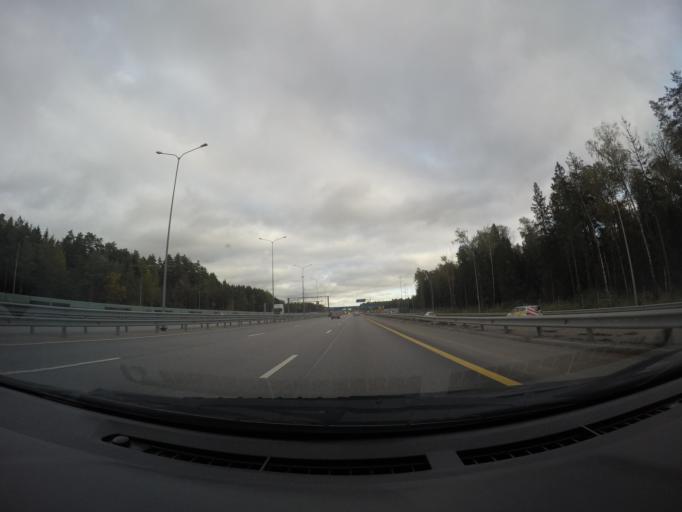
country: RU
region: Moskovskaya
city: Golitsyno
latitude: 55.5993
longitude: 36.9727
